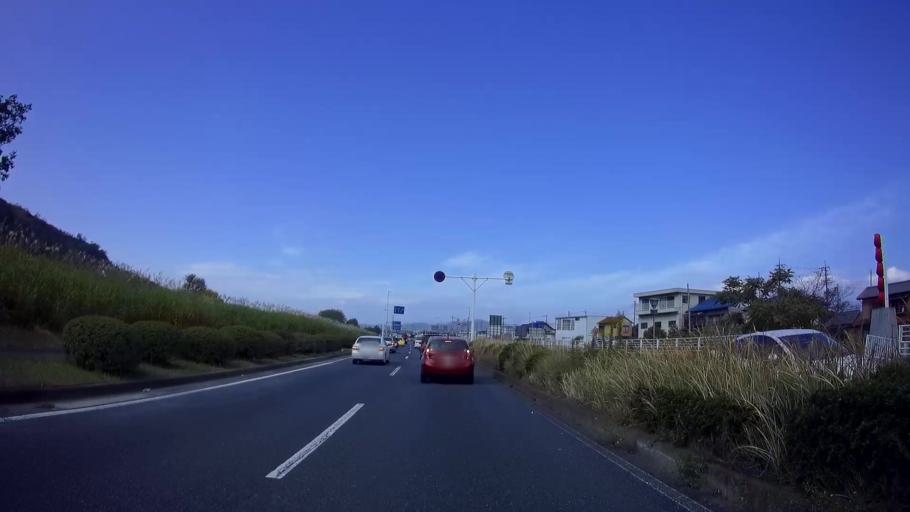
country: JP
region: Gunma
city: Takasaki
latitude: 36.3318
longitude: 138.9686
